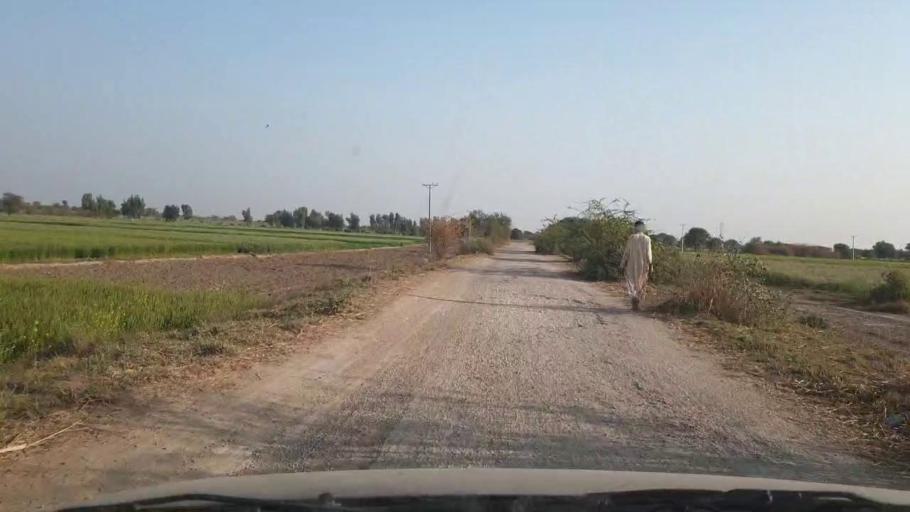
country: PK
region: Sindh
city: Samaro
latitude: 25.2775
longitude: 69.3614
